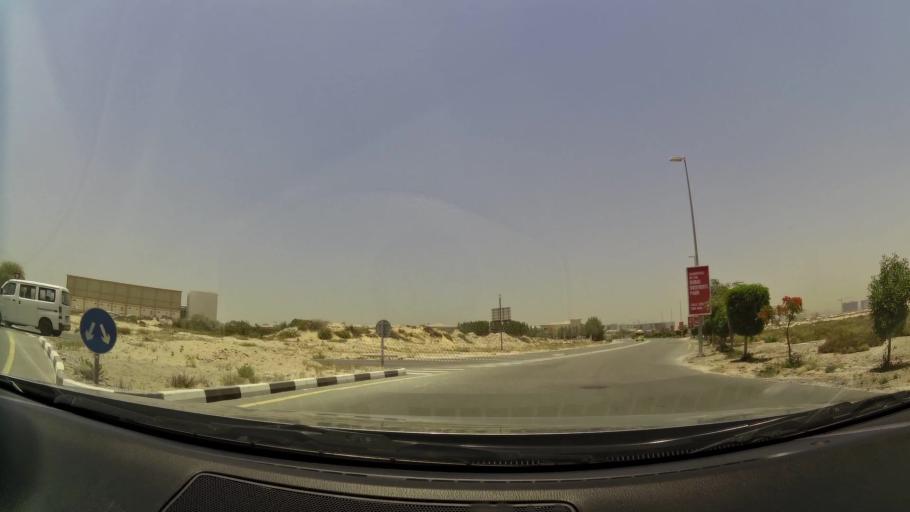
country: AE
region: Dubai
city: Dubai
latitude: 24.9886
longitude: 55.1662
